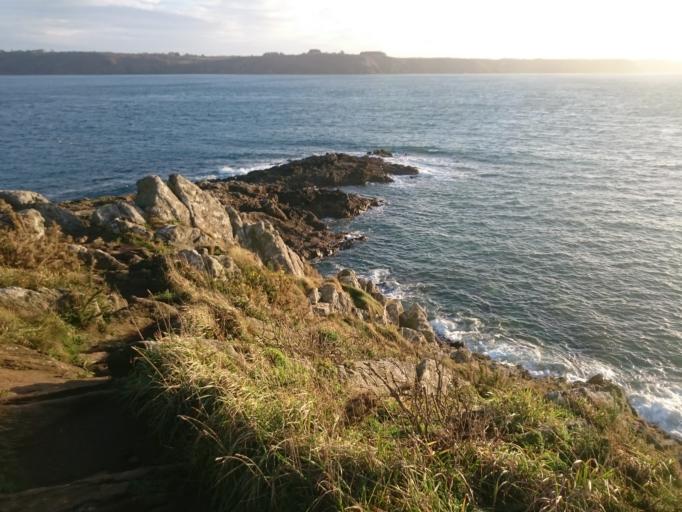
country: FR
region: Brittany
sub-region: Departement du Finistere
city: Roscanvel
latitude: 48.3549
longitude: -4.5590
